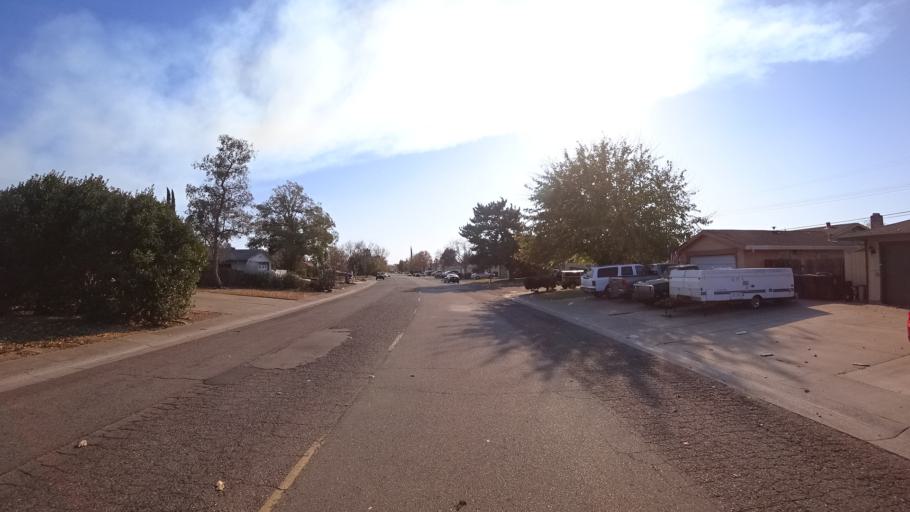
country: US
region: California
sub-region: Sacramento County
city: Antelope
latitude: 38.7048
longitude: -121.3210
